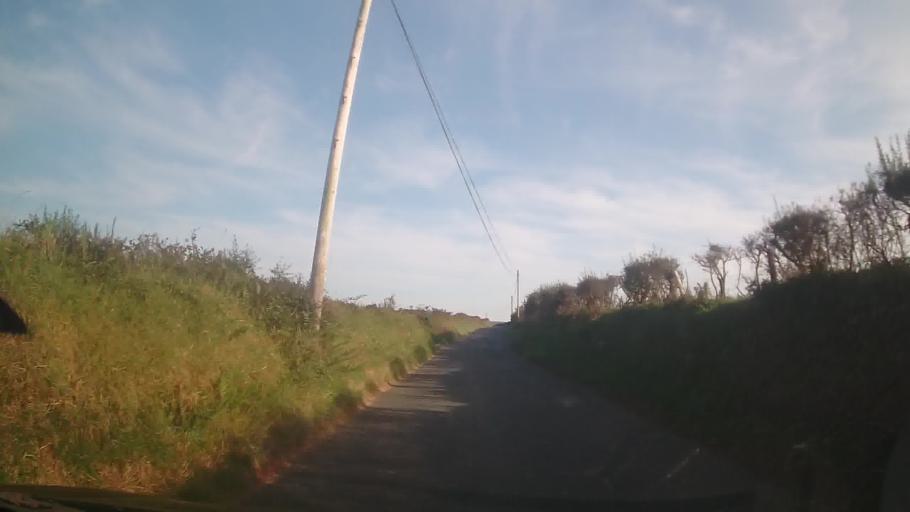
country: GB
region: Wales
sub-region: Pembrokeshire
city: Fishguard
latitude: 51.9875
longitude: -4.9590
